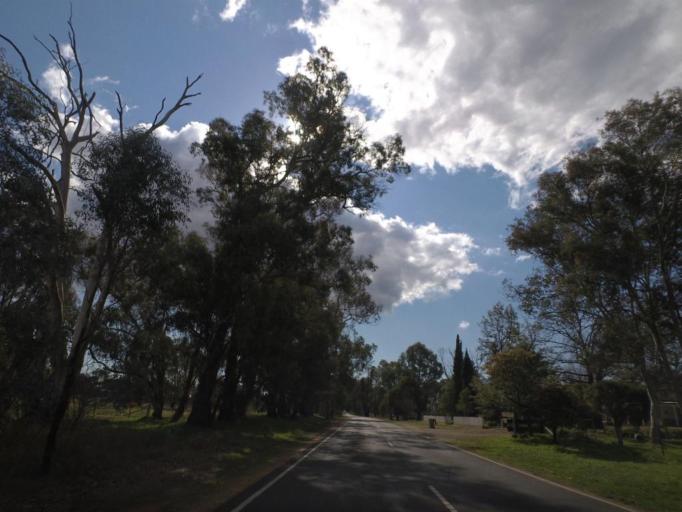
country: AU
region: New South Wales
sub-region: Corowa Shire
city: Howlong
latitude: -36.1692
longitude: 146.6078
